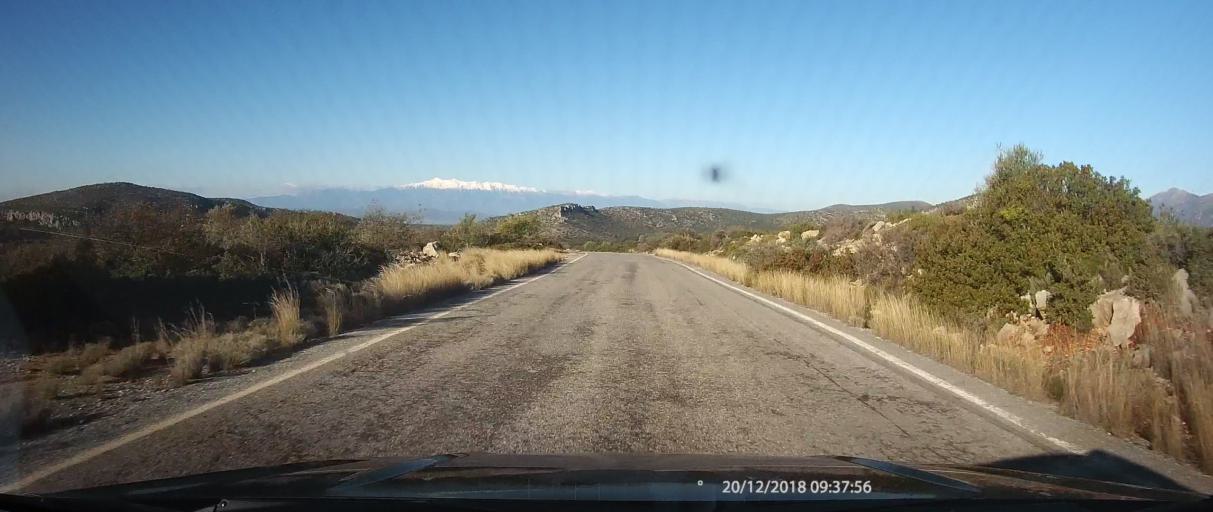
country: GR
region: Peloponnese
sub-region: Nomos Lakonias
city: Kato Glikovrisi
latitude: 36.9396
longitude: 22.7992
